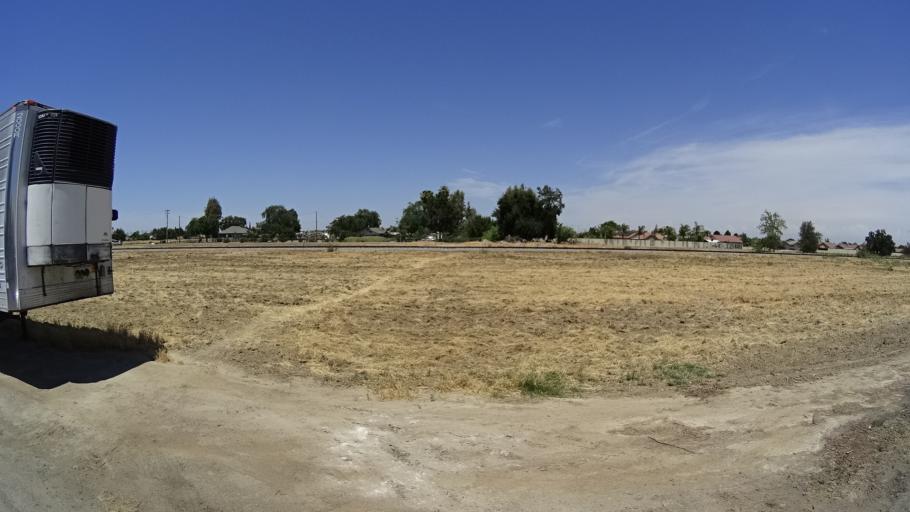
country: US
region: California
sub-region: Kings County
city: Armona
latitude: 36.3158
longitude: -119.7018
